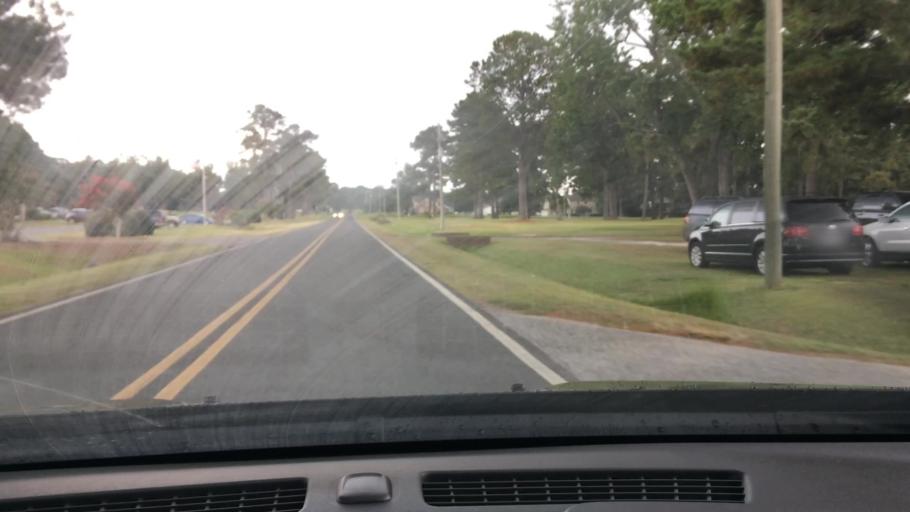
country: US
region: North Carolina
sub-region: Pitt County
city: Ayden
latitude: 35.4638
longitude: -77.3899
